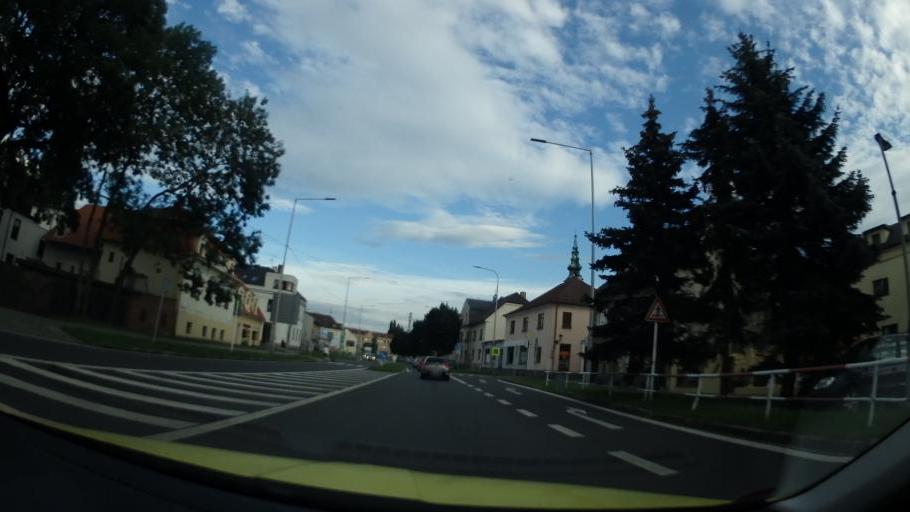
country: CZ
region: Moravskoslezsky
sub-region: Okres Novy Jicin
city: Novy Jicin
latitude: 49.5965
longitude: 18.0116
